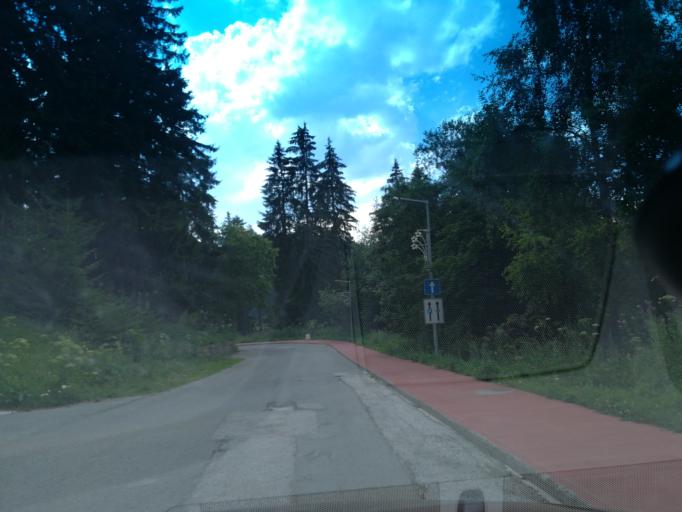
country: BG
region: Smolyan
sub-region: Obshtina Smolyan
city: Smolyan
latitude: 41.6595
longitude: 24.6980
